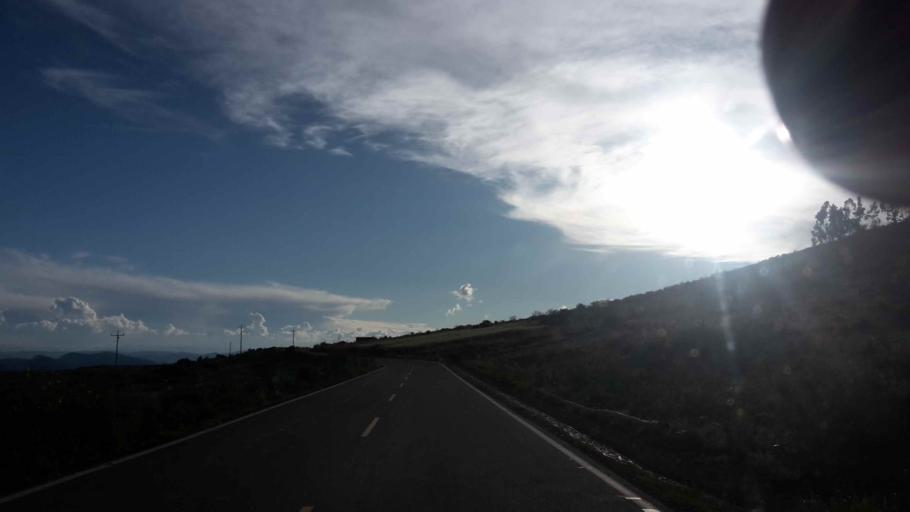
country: BO
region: Cochabamba
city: Arani
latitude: -17.5586
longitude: -65.7037
